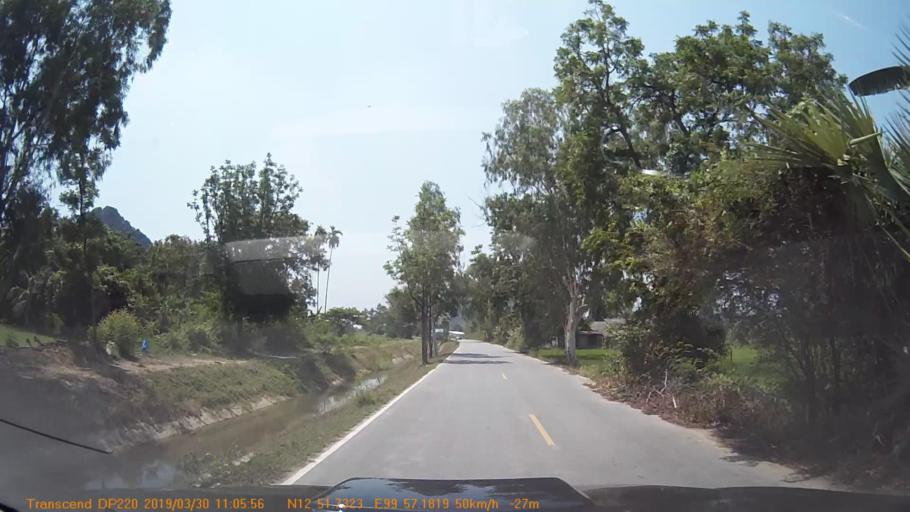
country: TH
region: Phetchaburi
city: Cha-am
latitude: 12.8620
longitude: 99.9530
